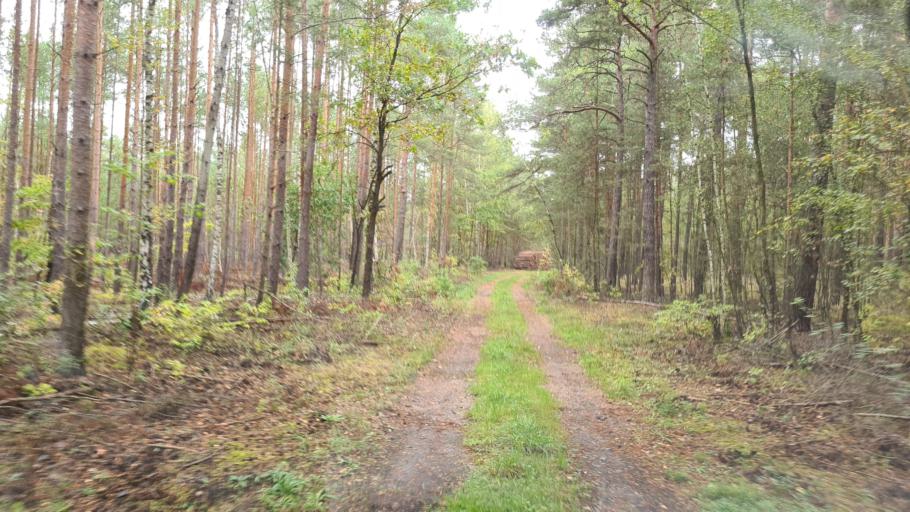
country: DE
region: Brandenburg
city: Altdobern
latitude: 51.6750
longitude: 14.1072
